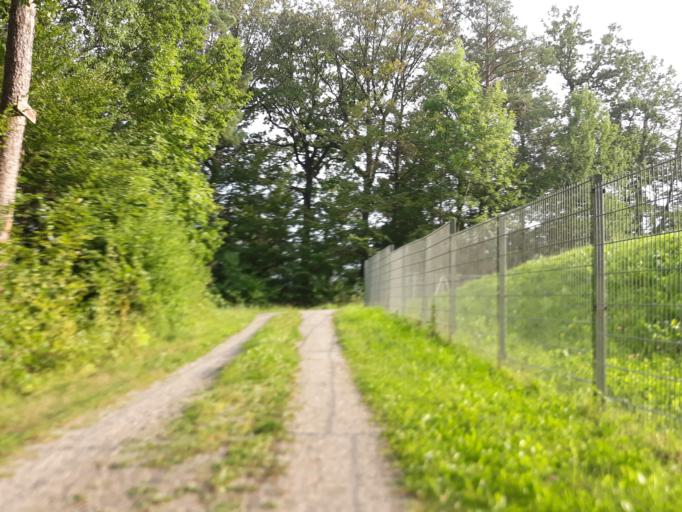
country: DE
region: Baden-Wuerttemberg
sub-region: Regierungsbezirk Stuttgart
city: Schonaich
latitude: 48.6684
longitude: 9.0538
